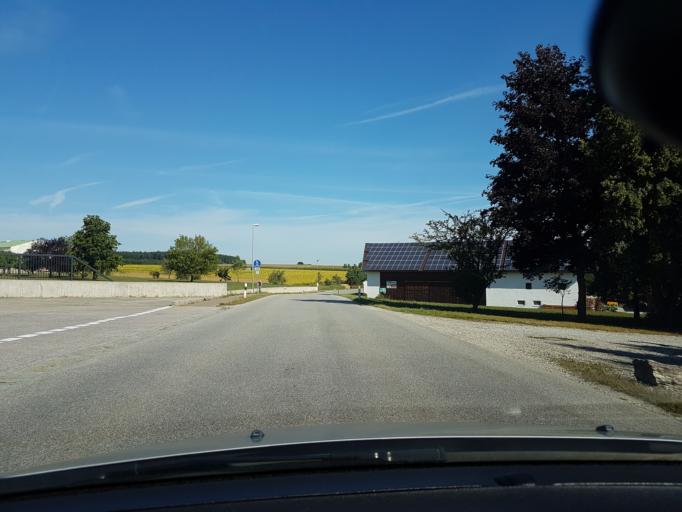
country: DE
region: Bavaria
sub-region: Lower Bavaria
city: Bodenkirchen
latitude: 48.3860
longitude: 12.3886
